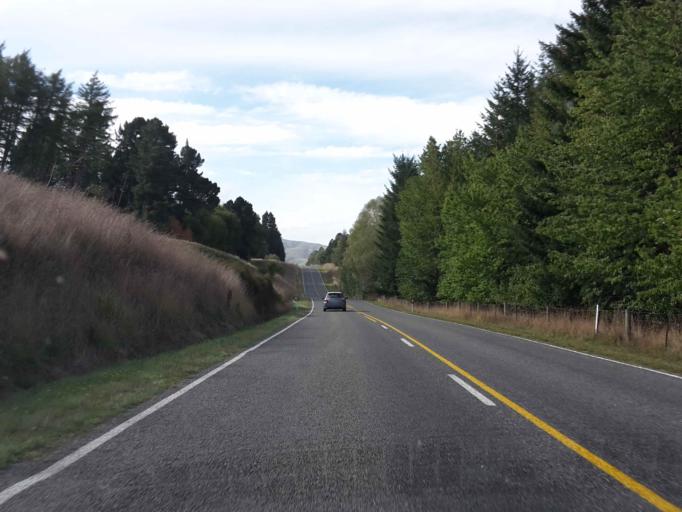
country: NZ
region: Canterbury
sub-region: Timaru District
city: Pleasant Point
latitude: -44.0543
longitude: 170.6772
